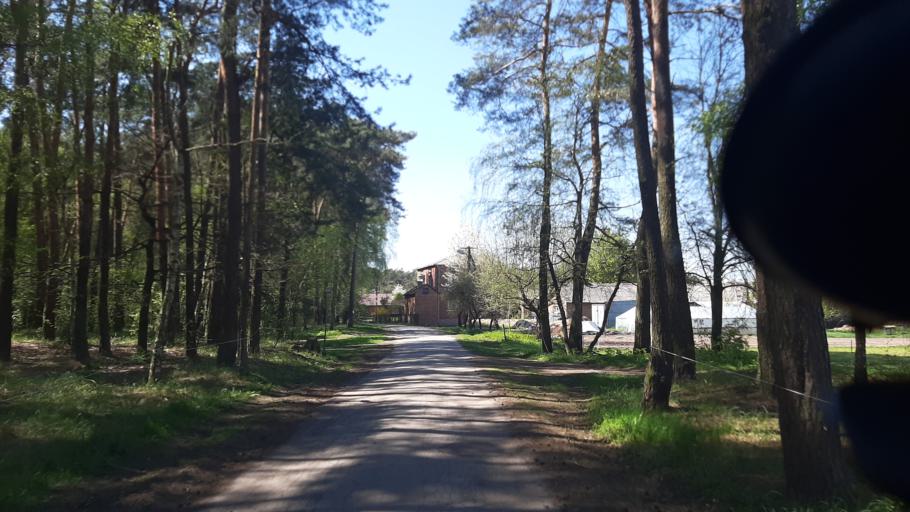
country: PL
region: Lublin Voivodeship
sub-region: Powiat lubartowski
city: Abramow
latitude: 51.4260
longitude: 22.2827
